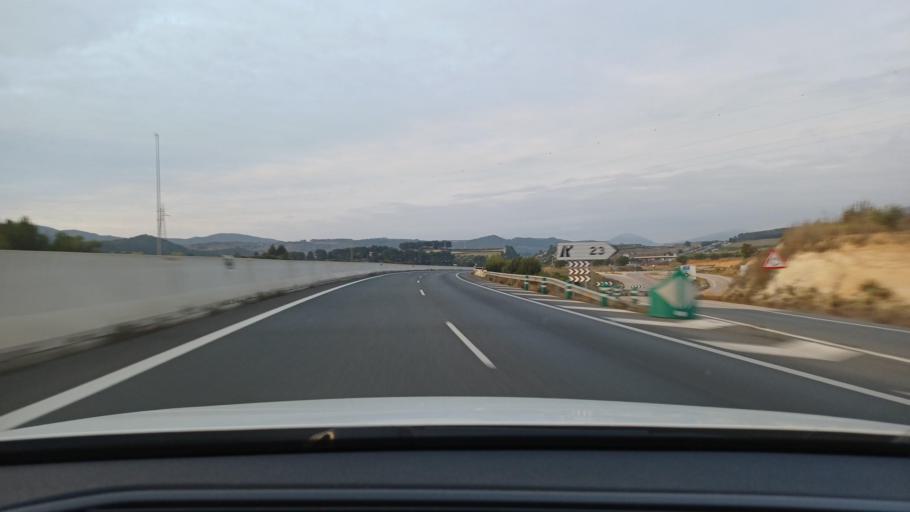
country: ES
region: Valencia
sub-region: Provincia de Valencia
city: Mogente
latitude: 38.8737
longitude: -0.7696
